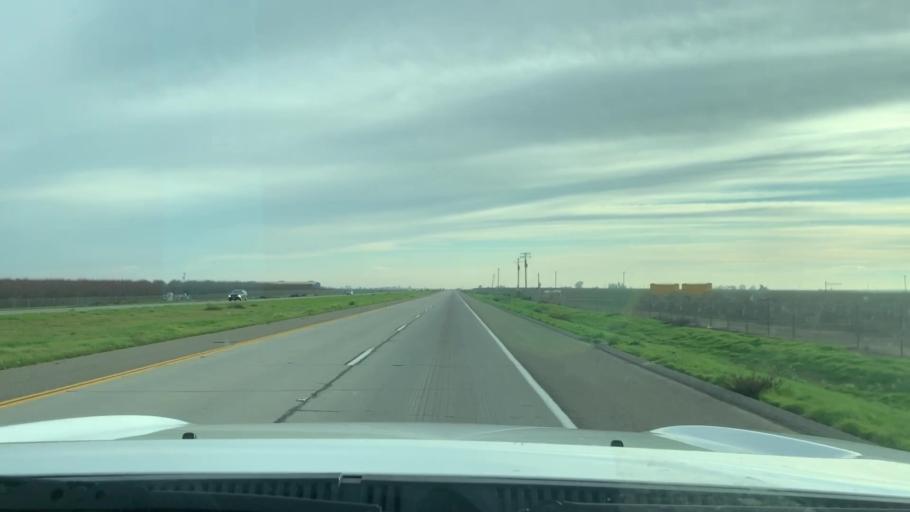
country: US
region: California
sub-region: Fresno County
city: Easton
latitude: 36.5868
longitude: -119.7862
